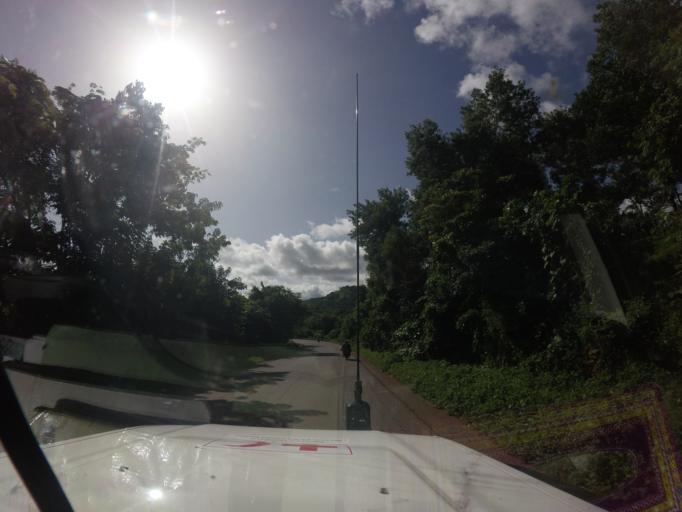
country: GN
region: Mamou
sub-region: Mamou Prefecture
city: Mamou
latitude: 10.3066
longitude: -12.2963
